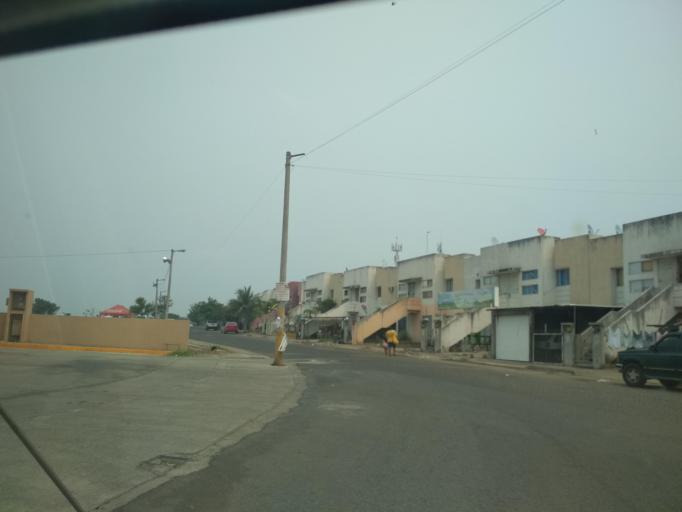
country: MX
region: Veracruz
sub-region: Veracruz
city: Fraccionamiento Geovillas los Pinos
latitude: 19.2244
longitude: -96.2425
